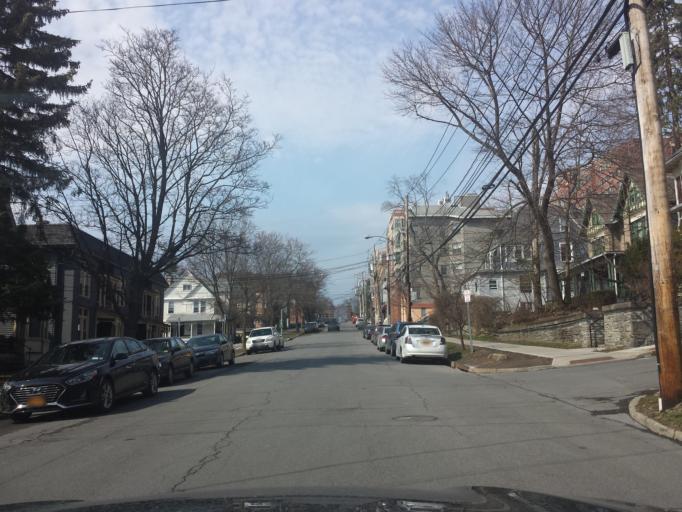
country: US
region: New York
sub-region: Tompkins County
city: East Ithaca
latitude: 42.4402
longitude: -76.4874
